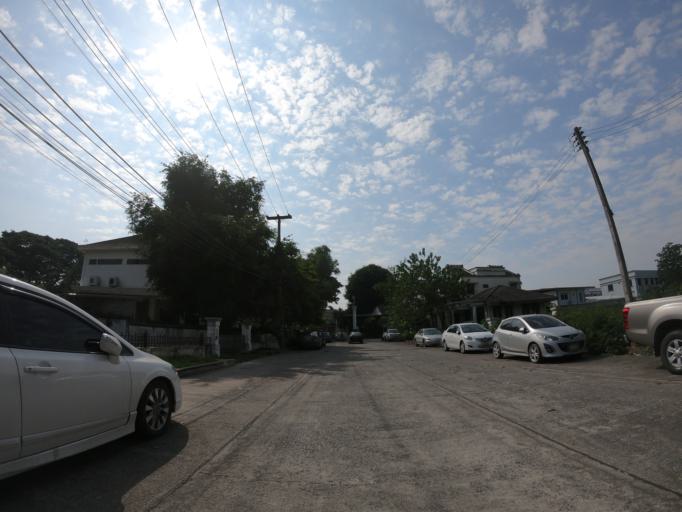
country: TH
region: Chiang Mai
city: Chiang Mai
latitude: 18.8030
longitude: 99.0071
